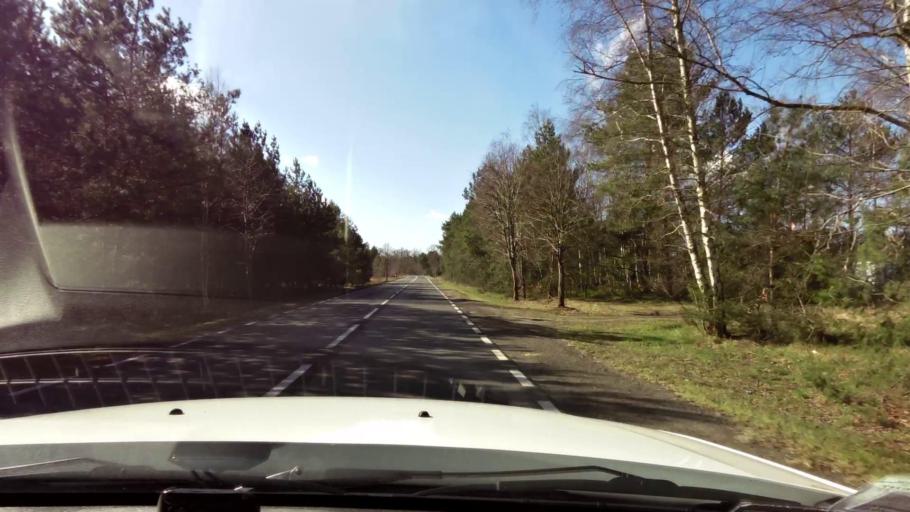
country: PL
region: West Pomeranian Voivodeship
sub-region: Powiat gryfinski
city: Gryfino
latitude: 53.2124
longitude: 14.4824
